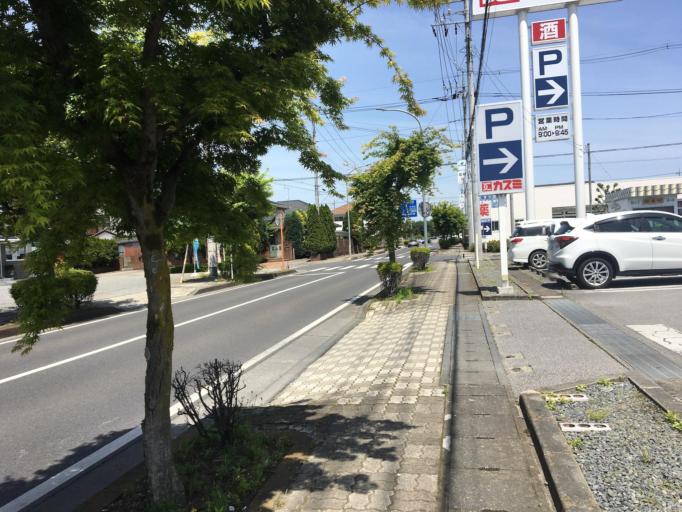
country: JP
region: Tochigi
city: Mibu
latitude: 36.4335
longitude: 139.8023
